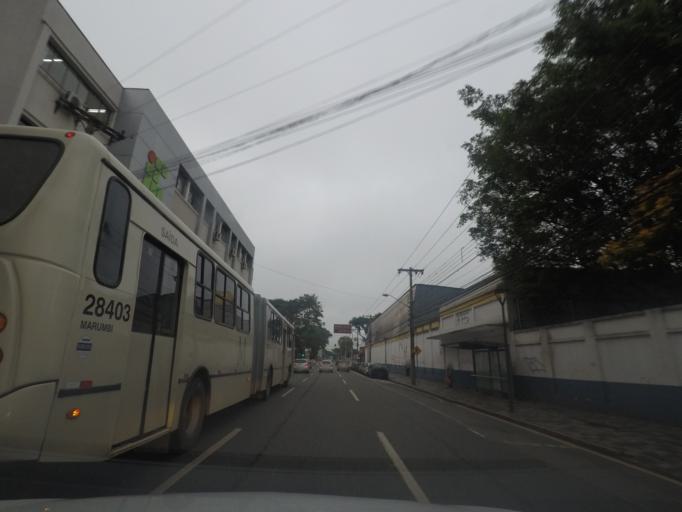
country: BR
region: Parana
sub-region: Curitiba
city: Curitiba
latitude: -25.4399
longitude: -49.2619
